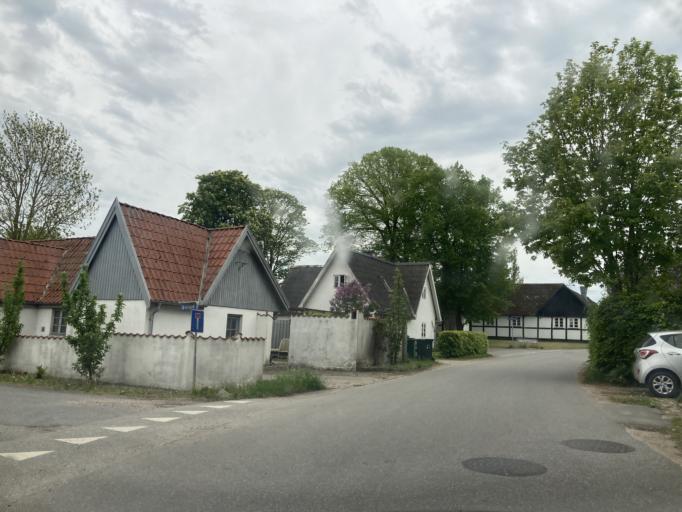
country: DK
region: Zealand
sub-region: Roskilde Kommune
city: Svogerslev
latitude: 55.6583
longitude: 11.9989
